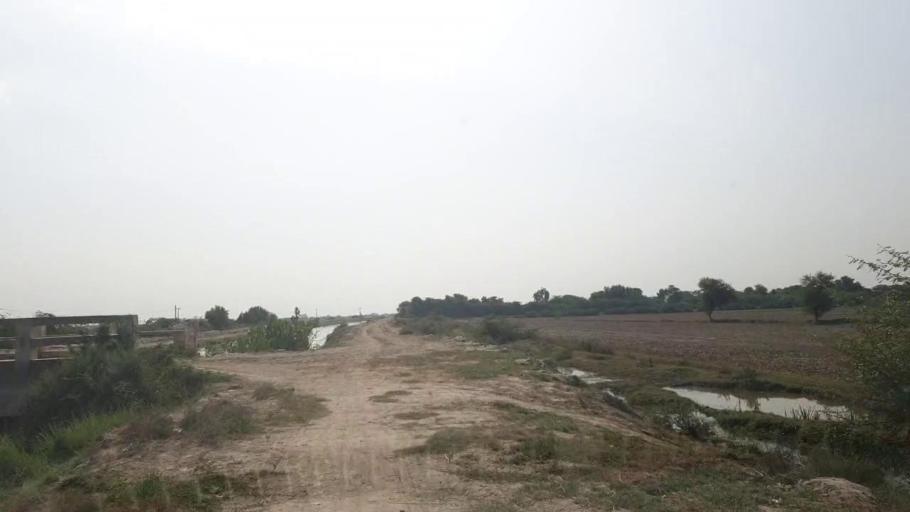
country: PK
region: Sindh
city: Badin
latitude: 24.5539
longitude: 68.8497
